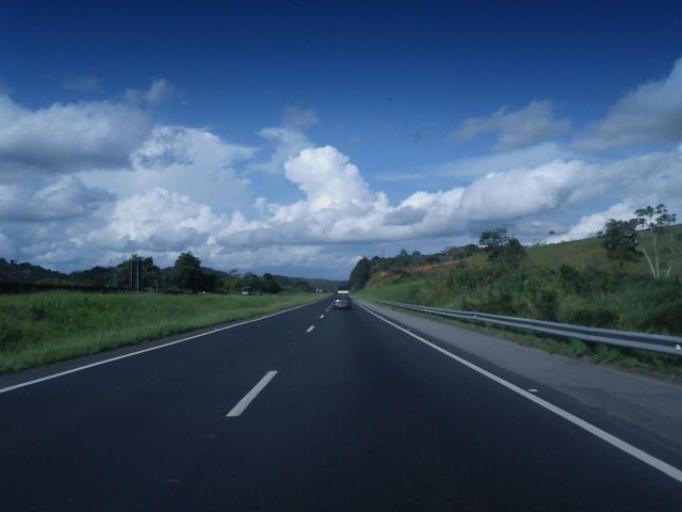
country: BR
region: Sao Paulo
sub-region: Registro
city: Registro
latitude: -24.4313
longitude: -47.7873
